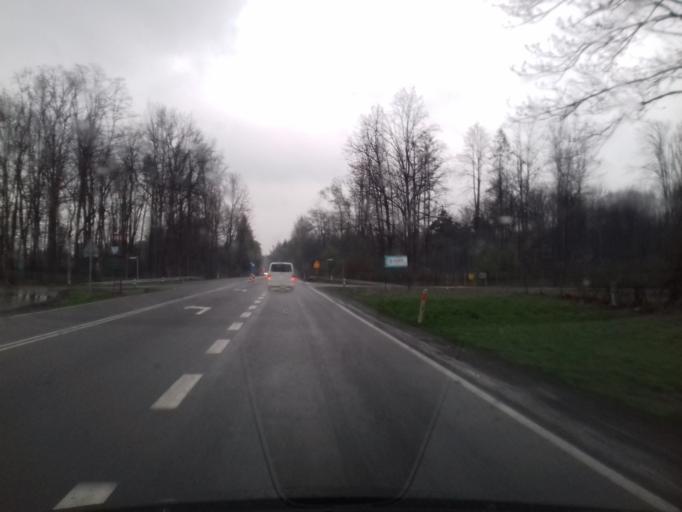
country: PL
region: Lesser Poland Voivodeship
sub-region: Powiat nowosadecki
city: Stary Sacz
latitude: 49.5604
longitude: 20.6557
